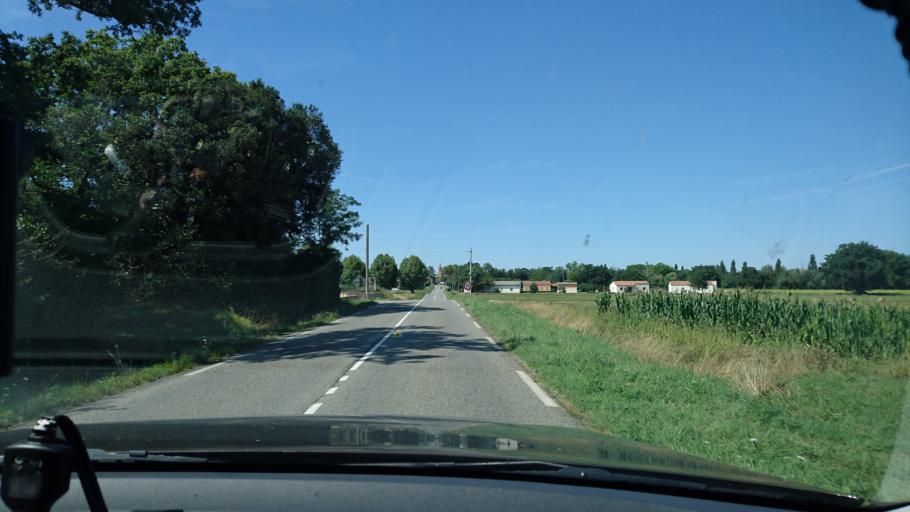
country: FR
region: Midi-Pyrenees
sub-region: Departement de l'Ariege
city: Lezat-sur-Leze
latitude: 43.2664
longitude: 1.3524
